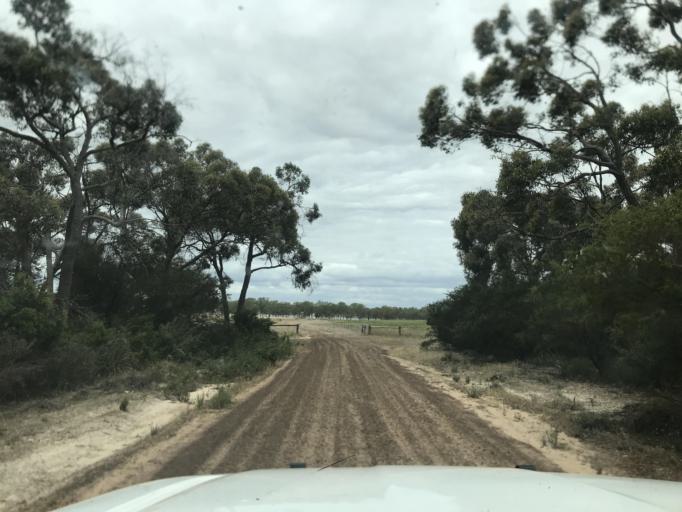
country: AU
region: South Australia
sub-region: Naracoorte and Lucindale
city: Naracoorte
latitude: -36.9227
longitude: 141.3313
